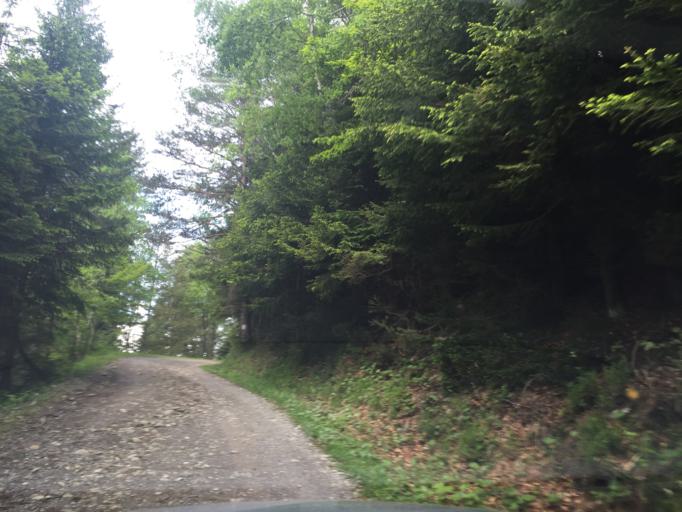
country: FR
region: Rhone-Alpes
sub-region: Departement de la Savoie
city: La Rochette
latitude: 45.4400
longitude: 6.1692
